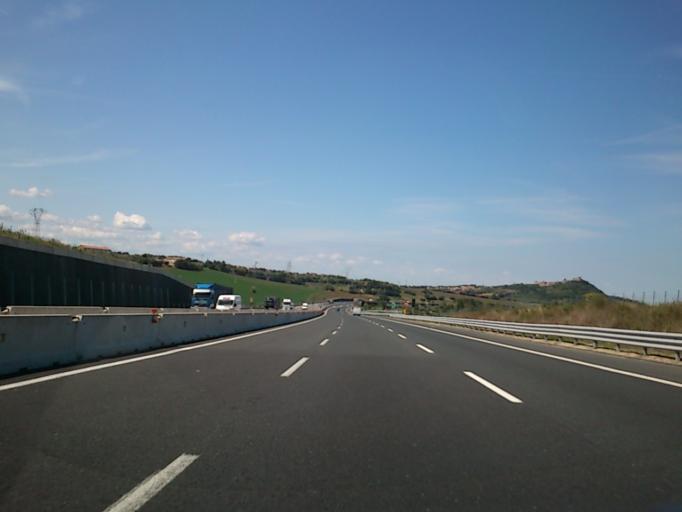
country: IT
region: The Marches
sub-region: Provincia di Pesaro e Urbino
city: Gradara
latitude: 43.9255
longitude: 12.8054
